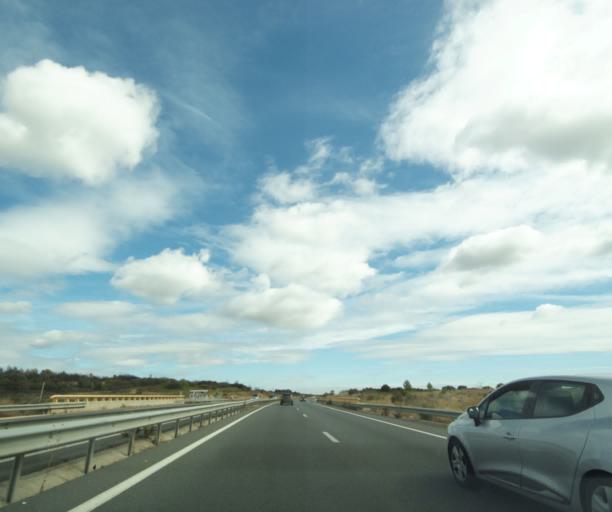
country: FR
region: Languedoc-Roussillon
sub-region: Departement de l'Herault
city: Murviel-les-Montpellier
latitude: 43.6329
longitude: 3.7286
